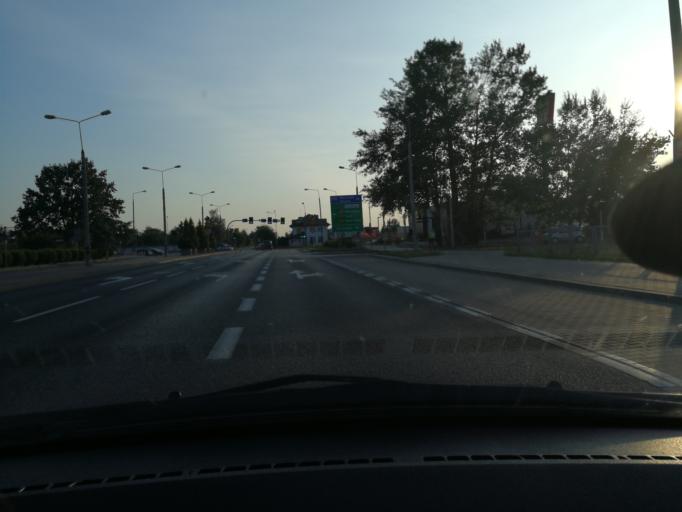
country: PL
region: Lodz Voivodeship
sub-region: Skierniewice
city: Skierniewice
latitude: 51.9716
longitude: 20.1488
